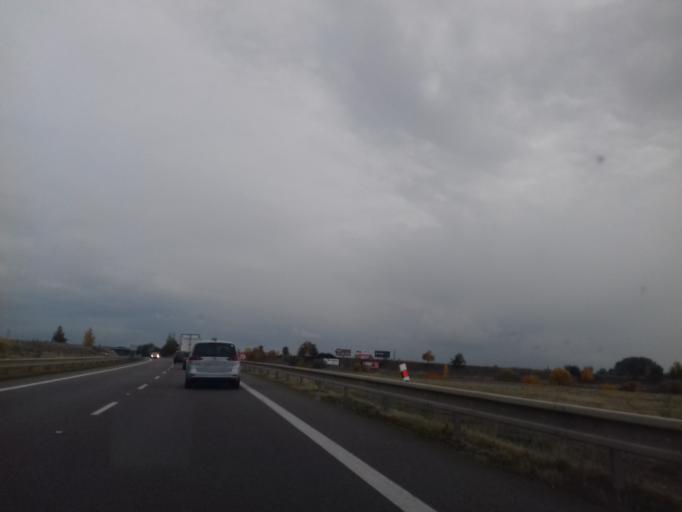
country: CZ
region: Pardubicky
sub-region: Okres Chrudim
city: Chrudim
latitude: 49.9899
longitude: 15.7692
